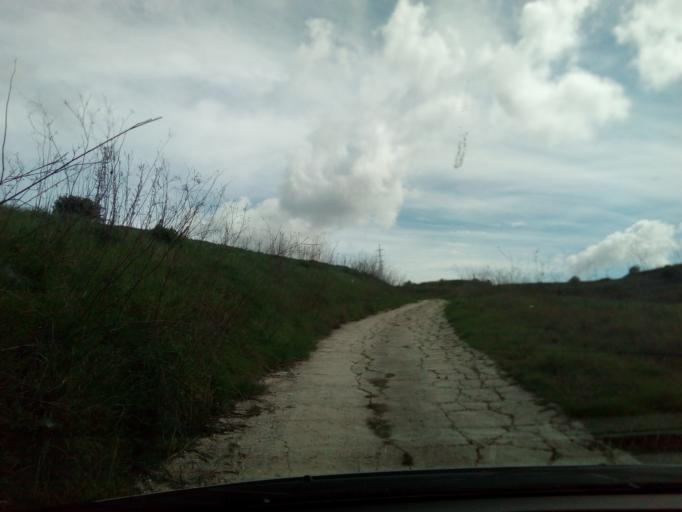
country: CY
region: Pafos
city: Tala
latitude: 34.8999
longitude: 32.4911
